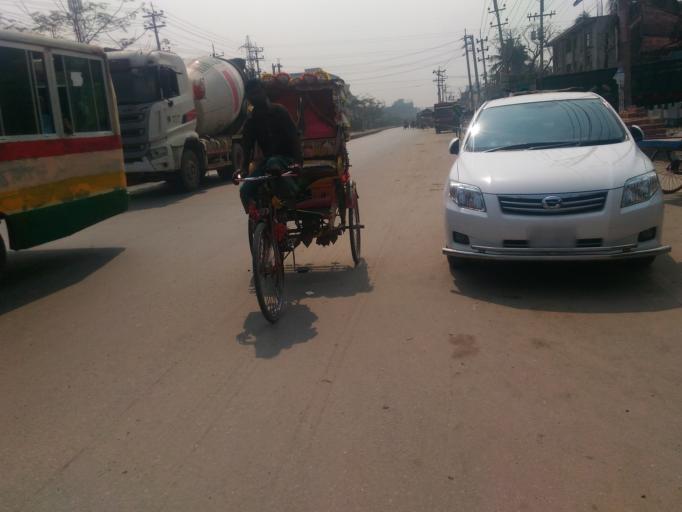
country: BD
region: Dhaka
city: Tungi
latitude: 23.9997
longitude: 90.3826
